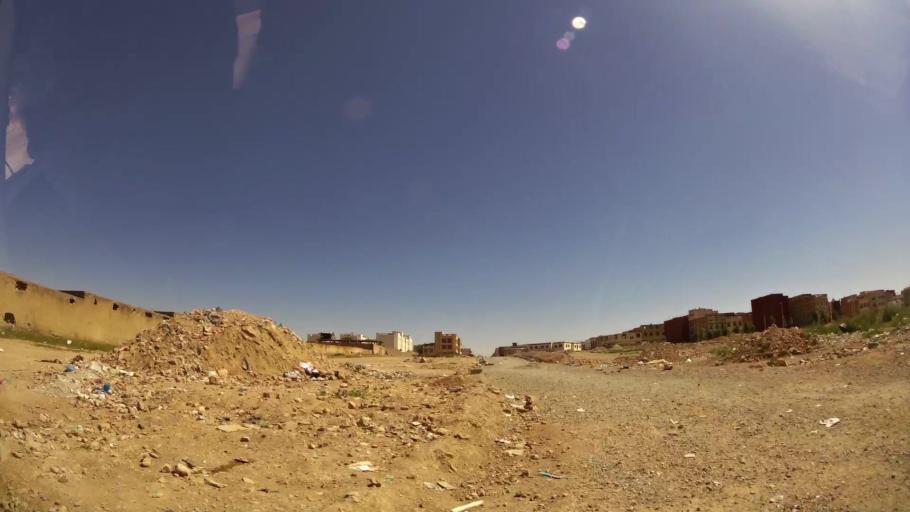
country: MA
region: Oriental
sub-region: Oujda-Angad
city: Oujda
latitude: 34.6624
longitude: -1.8683
